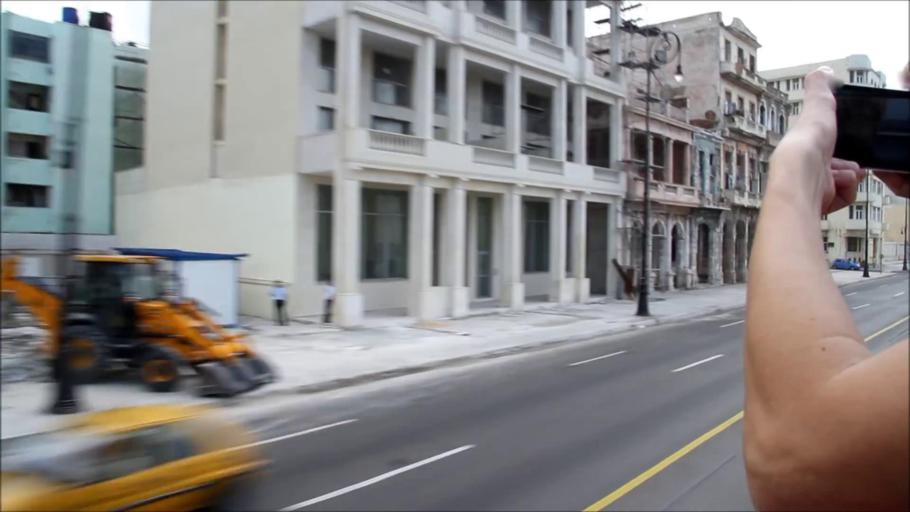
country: CU
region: La Habana
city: Centro Habana
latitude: 23.1431
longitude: -82.3623
